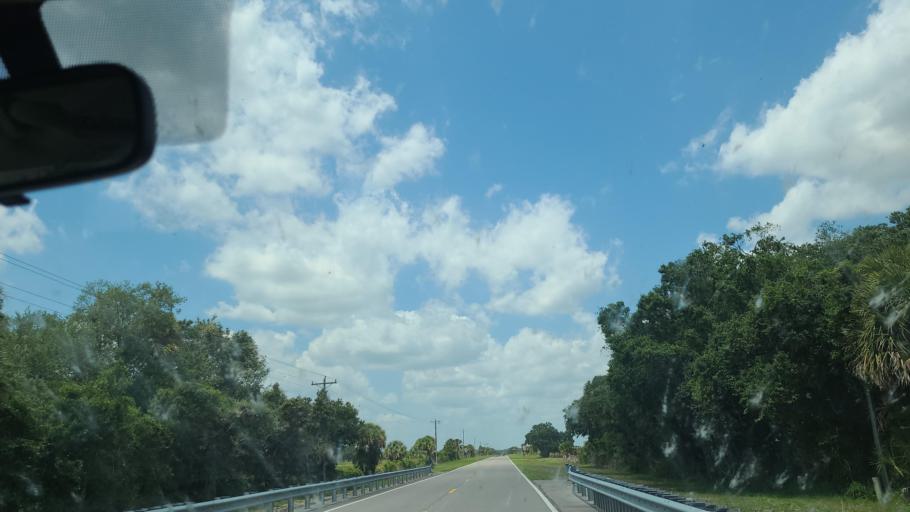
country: US
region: Florida
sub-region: Okeechobee County
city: Cypress Quarters
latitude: 27.3946
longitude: -80.8948
